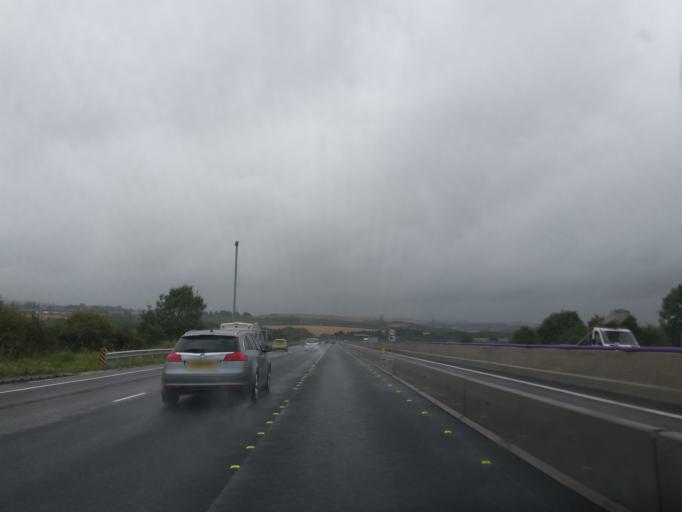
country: GB
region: England
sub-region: Derbyshire
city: Barlborough
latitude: 53.2712
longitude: -1.3036
